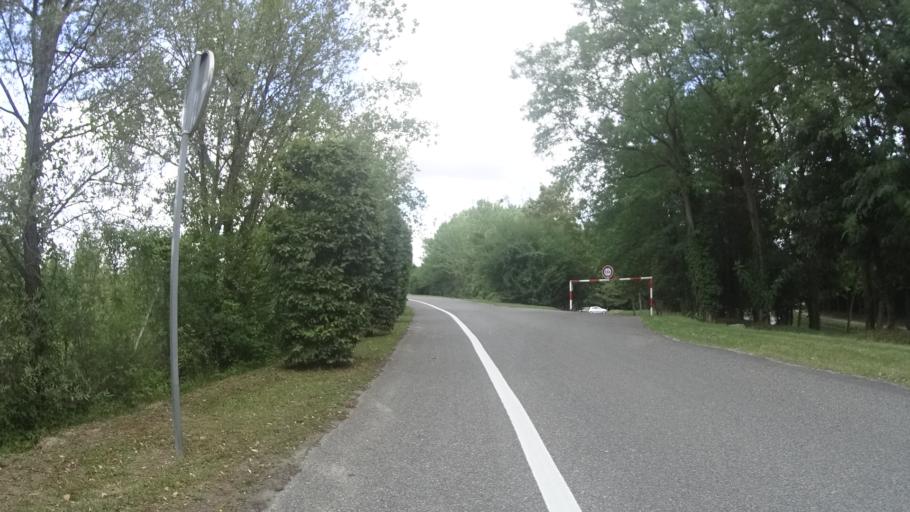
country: FR
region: Ile-de-France
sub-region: Departement de Seine-et-Marne
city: Claye-Souilly
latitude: 48.9586
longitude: 2.6692
